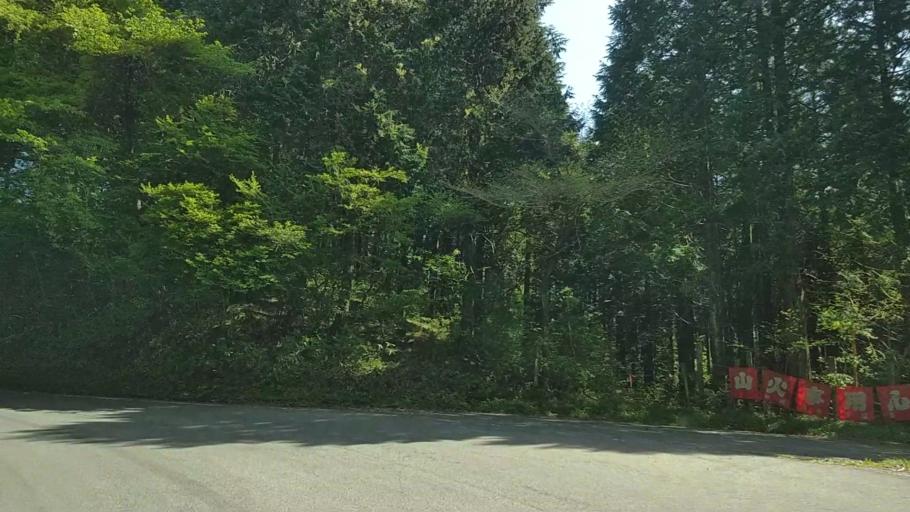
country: JP
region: Shizuoka
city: Gotemba
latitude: 35.2683
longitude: 138.9625
